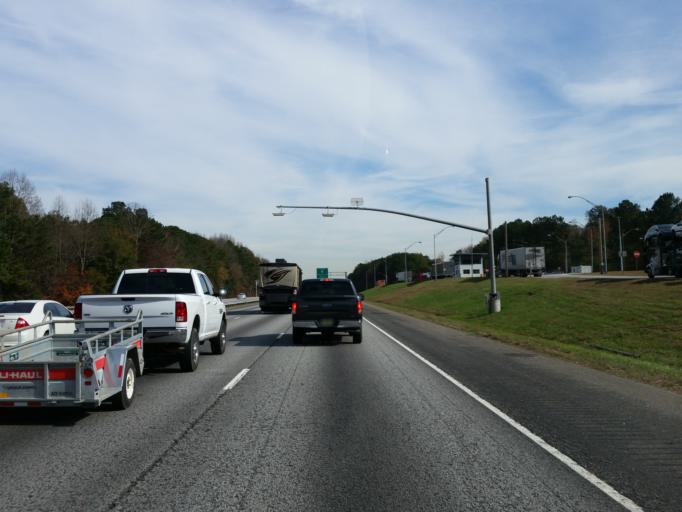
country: US
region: Georgia
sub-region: Douglas County
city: Lithia Springs
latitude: 33.7726
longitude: -84.6324
